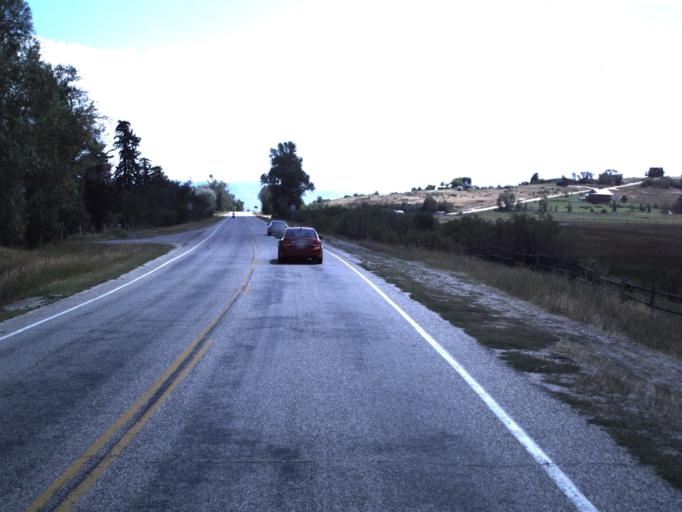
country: US
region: Idaho
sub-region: Bear Lake County
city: Paris
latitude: 41.9830
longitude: -111.4093
